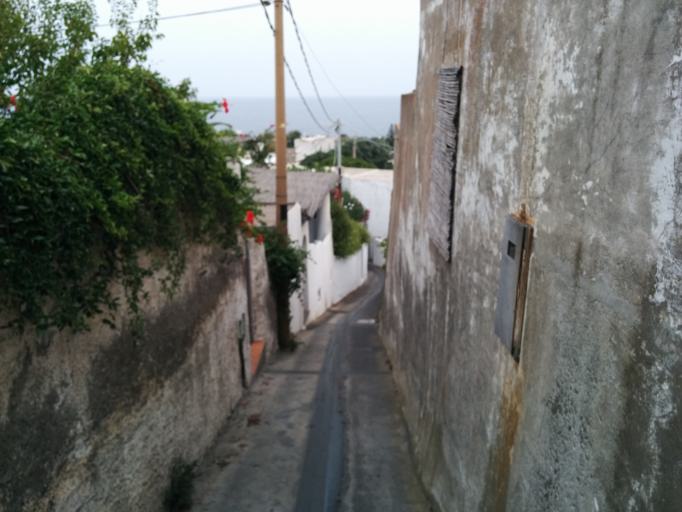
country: IT
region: Sicily
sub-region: Messina
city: Canneto
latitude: 38.8036
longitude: 15.2386
